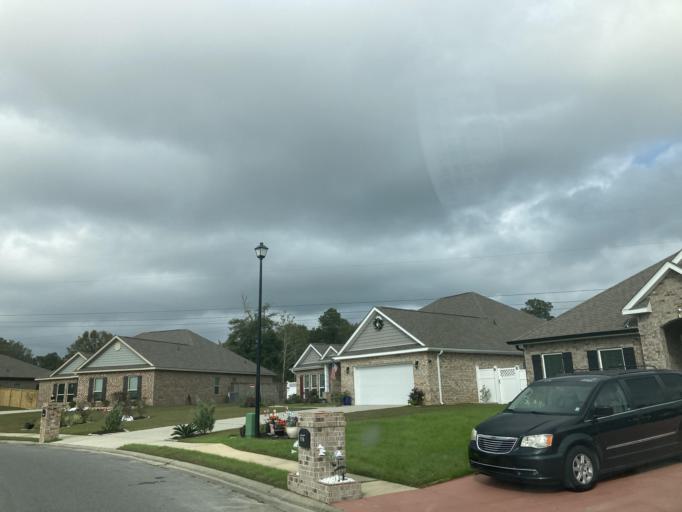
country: US
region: Mississippi
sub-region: Harrison County
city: D'Iberville
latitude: 30.4776
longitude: -88.9861
